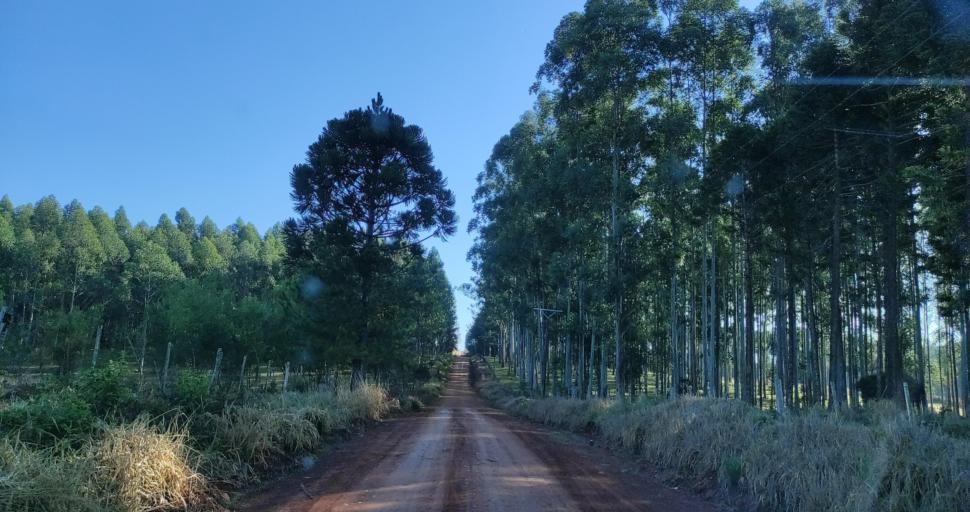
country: AR
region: Misiones
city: Puerto Rico
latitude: -26.8648
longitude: -55.0151
